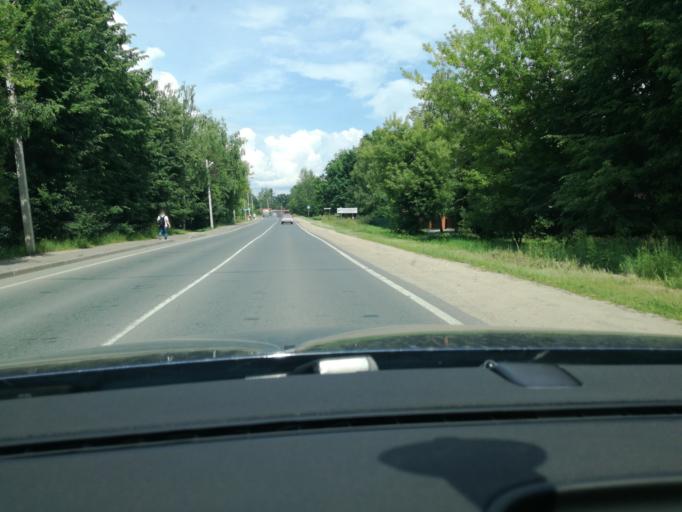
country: RU
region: Moskovskaya
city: Semkhoz
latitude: 56.2830
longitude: 38.0599
